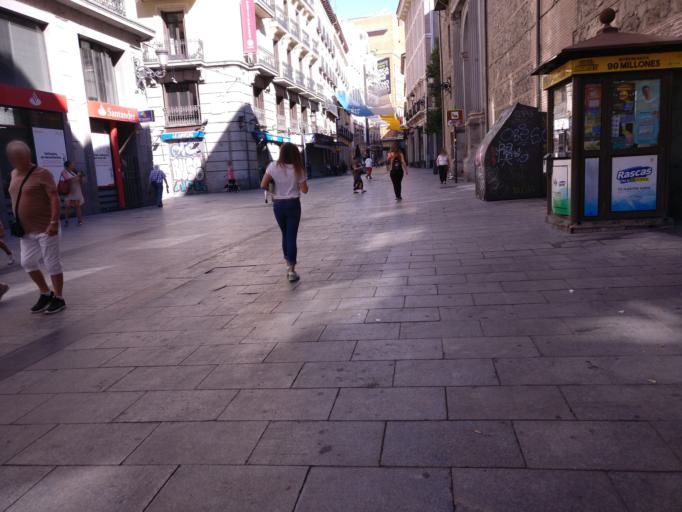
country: ES
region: Madrid
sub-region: Provincia de Madrid
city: City Center
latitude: 40.4180
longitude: -3.7041
